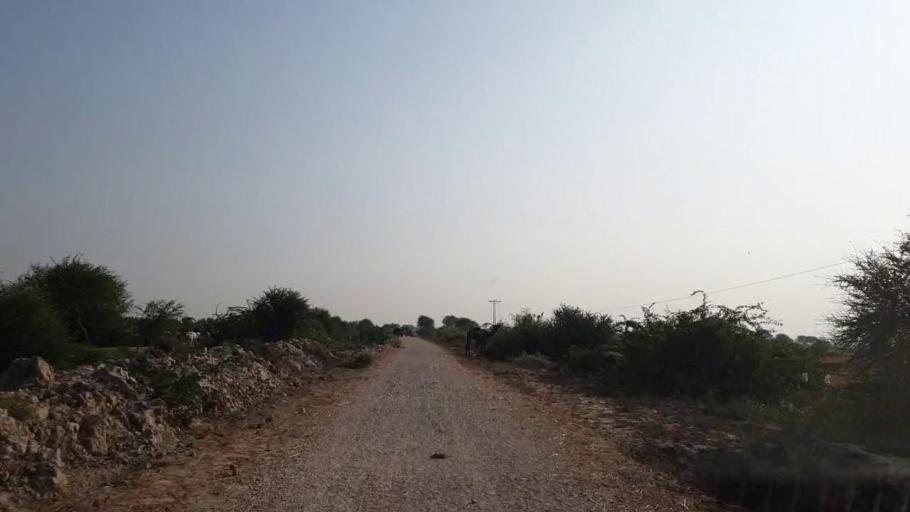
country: PK
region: Sindh
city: Bulri
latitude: 24.9877
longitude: 68.3767
